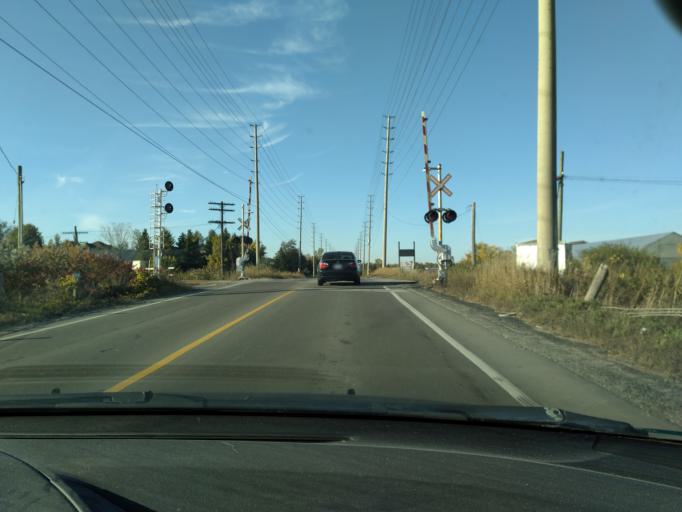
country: CA
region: Ontario
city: Brampton
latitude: 43.8644
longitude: -79.7050
